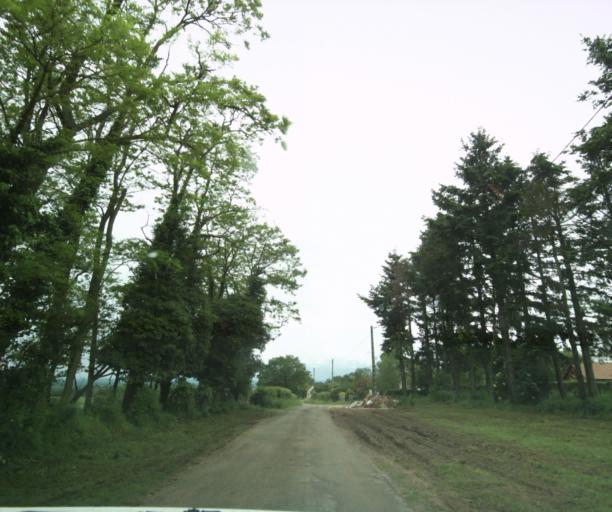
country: FR
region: Bourgogne
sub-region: Departement de Saone-et-Loire
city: Charolles
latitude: 46.4924
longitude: 4.2728
